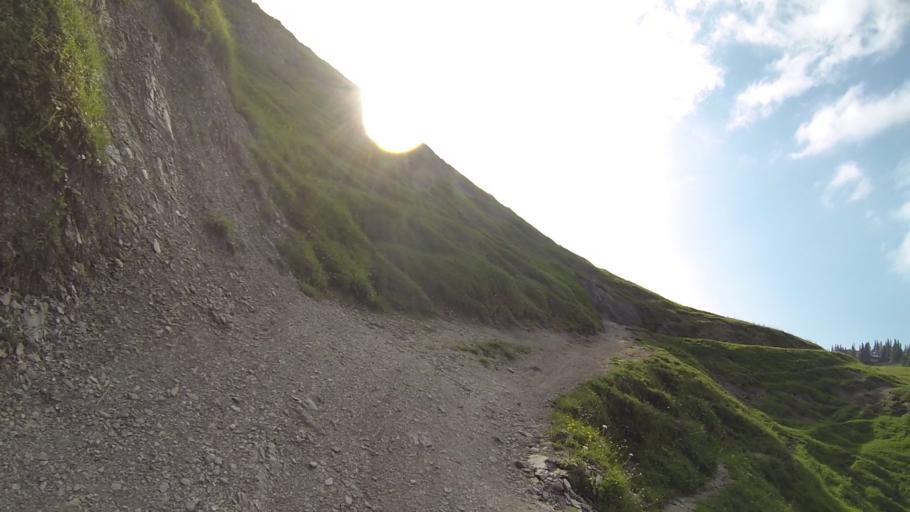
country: DE
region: Bavaria
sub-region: Swabia
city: Nesselwang
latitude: 47.5939
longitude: 10.4982
